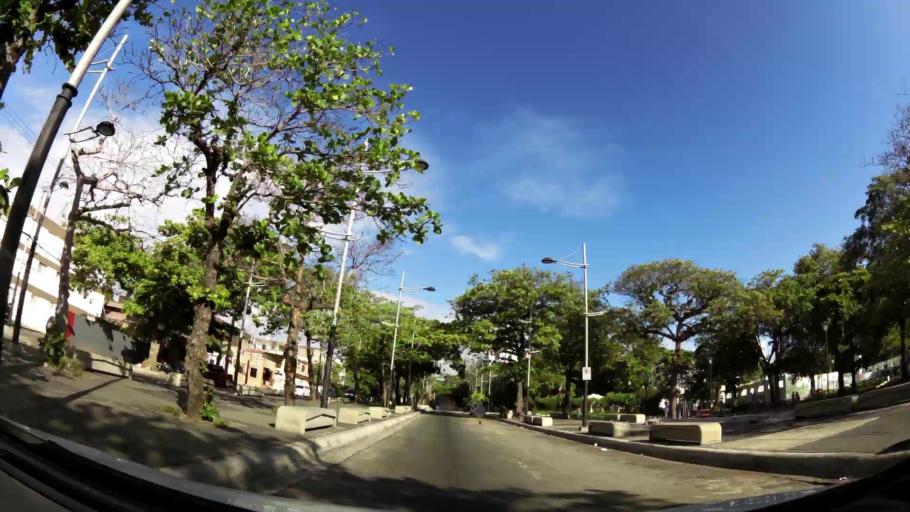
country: DO
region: Nacional
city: Ciudad Nueva
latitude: 18.4653
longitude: -69.8945
